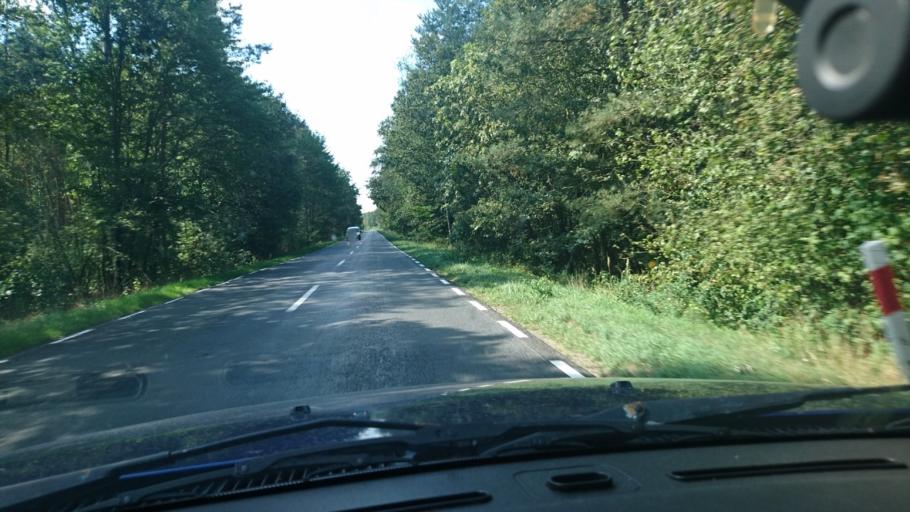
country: PL
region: Greater Poland Voivodeship
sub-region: Powiat krotoszynski
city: Sulmierzyce
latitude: 51.5996
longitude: 17.5984
